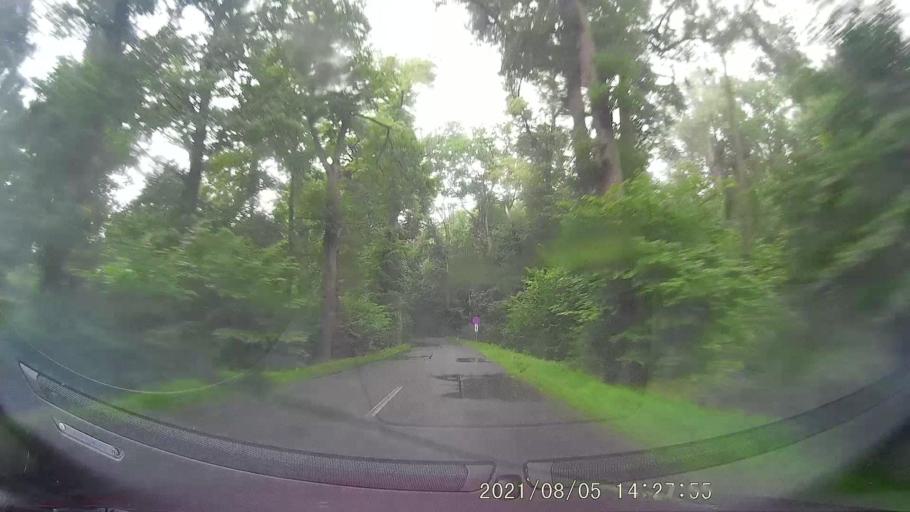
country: PL
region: Opole Voivodeship
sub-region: Powiat nyski
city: Korfantow
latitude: 50.4908
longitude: 17.5888
